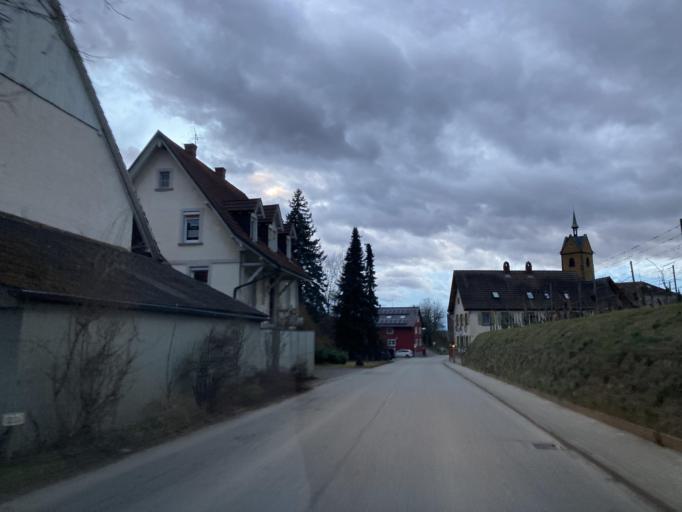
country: DE
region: Baden-Wuerttemberg
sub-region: Freiburg Region
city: Vogtsburg
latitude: 48.0855
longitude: 7.6142
